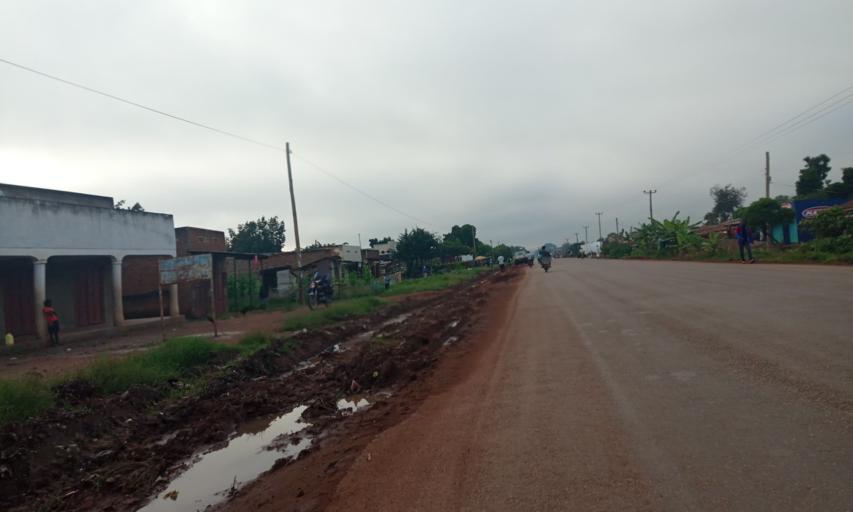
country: UG
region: Eastern Region
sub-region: Mbale District
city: Mbale
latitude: 1.1167
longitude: 34.1705
